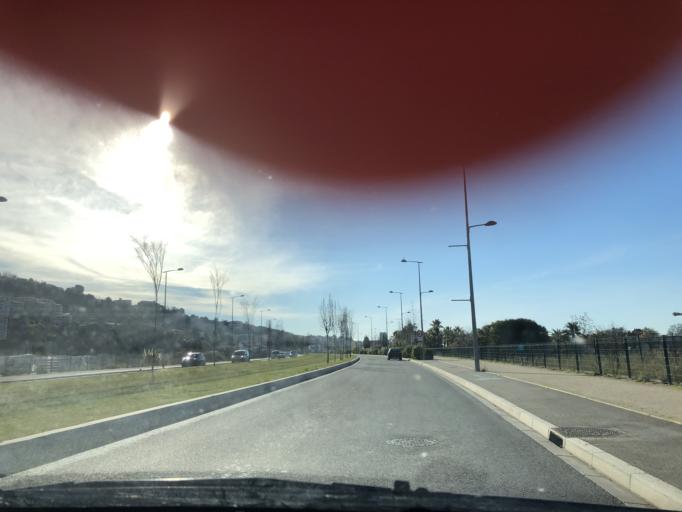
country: FR
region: Provence-Alpes-Cote d'Azur
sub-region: Departement des Alpes-Maritimes
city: Saint-Laurent-du-Var
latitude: 43.6971
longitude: 7.1966
